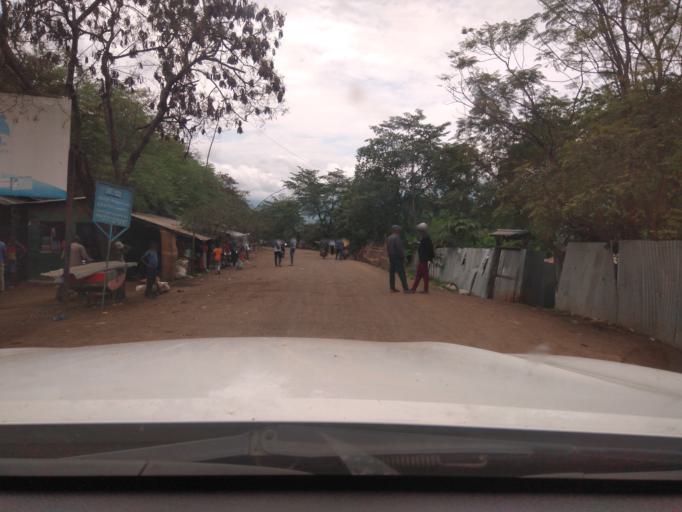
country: ET
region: Southern Nations, Nationalities, and People's Region
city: Felege Neway
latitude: 6.3972
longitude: 37.0846
